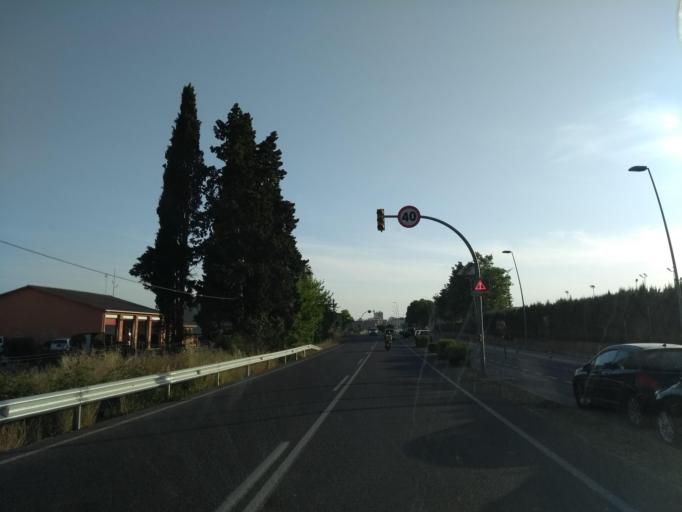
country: ES
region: Balearic Islands
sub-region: Illes Balears
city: Inca
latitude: 39.7280
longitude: 2.9255
